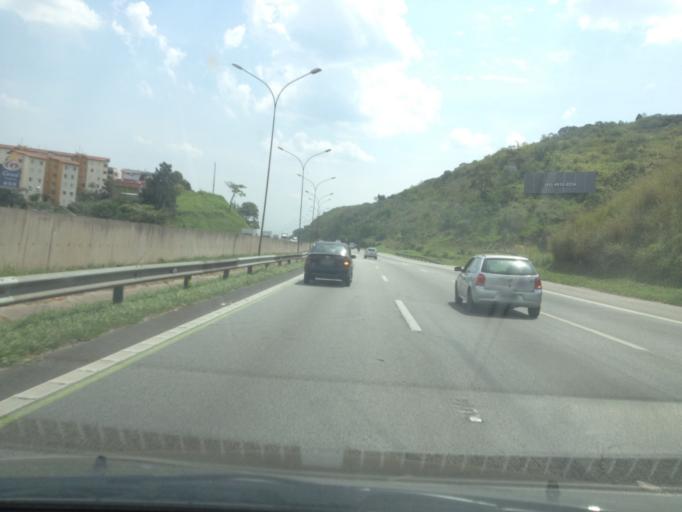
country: BR
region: Sao Paulo
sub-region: Barueri
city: Barueri
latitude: -23.5064
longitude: -46.8970
